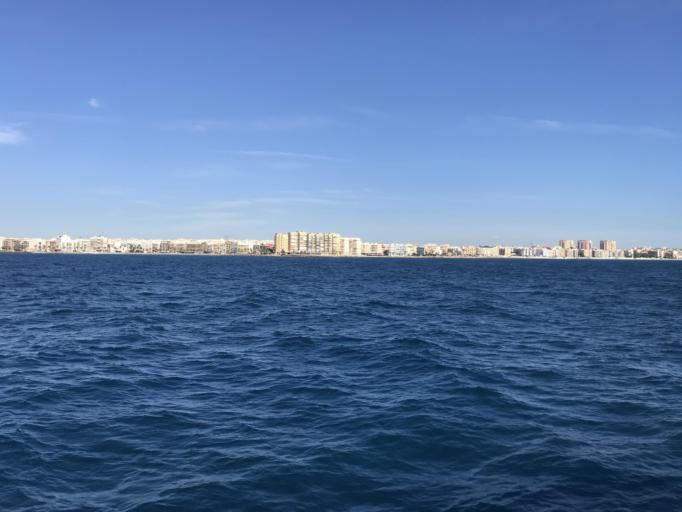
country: ES
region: Valencia
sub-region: Provincia de Alicante
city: Torrevieja
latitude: 37.9686
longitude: -0.6621
